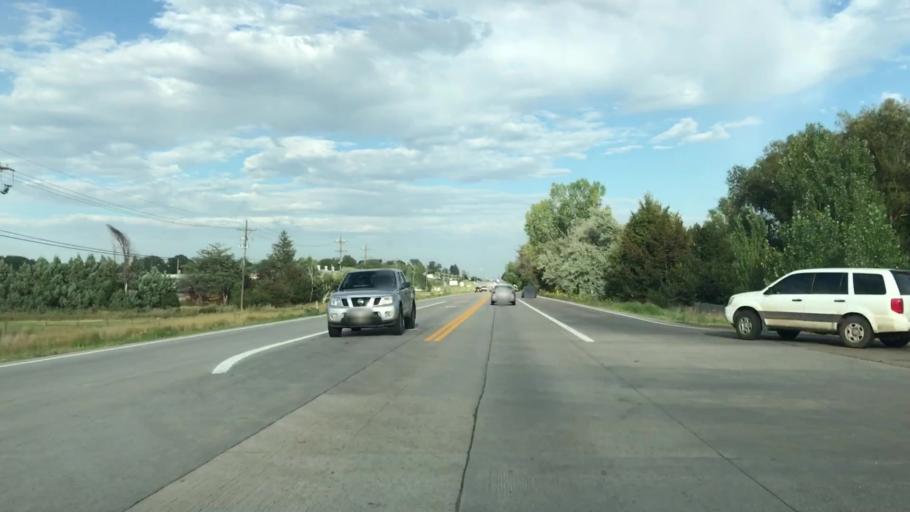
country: US
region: Colorado
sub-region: Boulder County
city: Longmont
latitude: 40.2031
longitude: -105.1168
